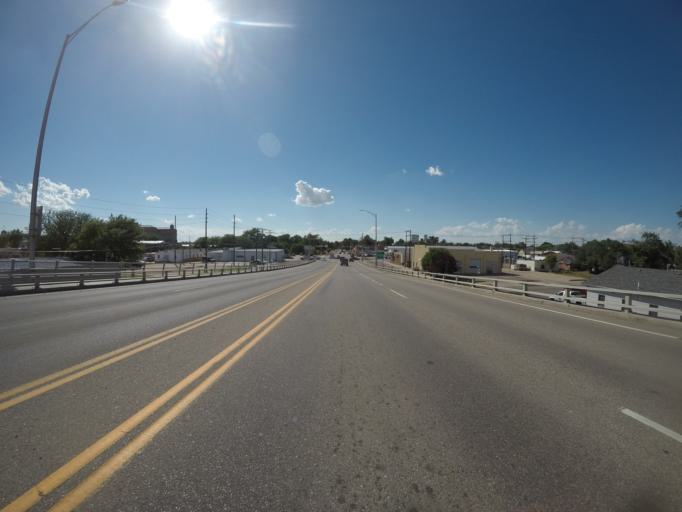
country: US
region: Colorado
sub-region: Logan County
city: Sterling
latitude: 40.6258
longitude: -103.2051
